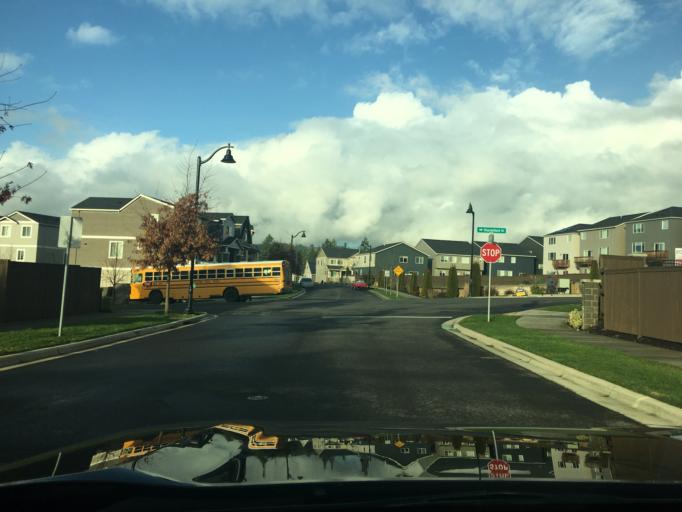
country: US
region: Oregon
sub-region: Washington County
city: Bethany
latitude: 45.5740
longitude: -122.8535
